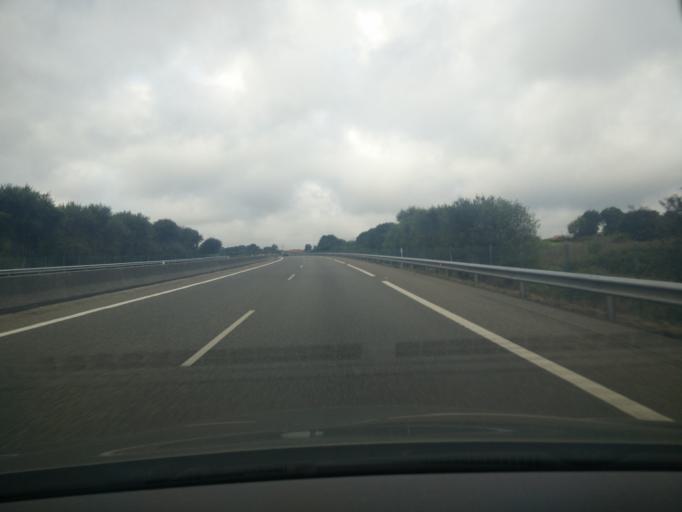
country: ES
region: Galicia
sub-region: Provincia da Coruna
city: Laracha
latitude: 43.2629
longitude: -8.5923
